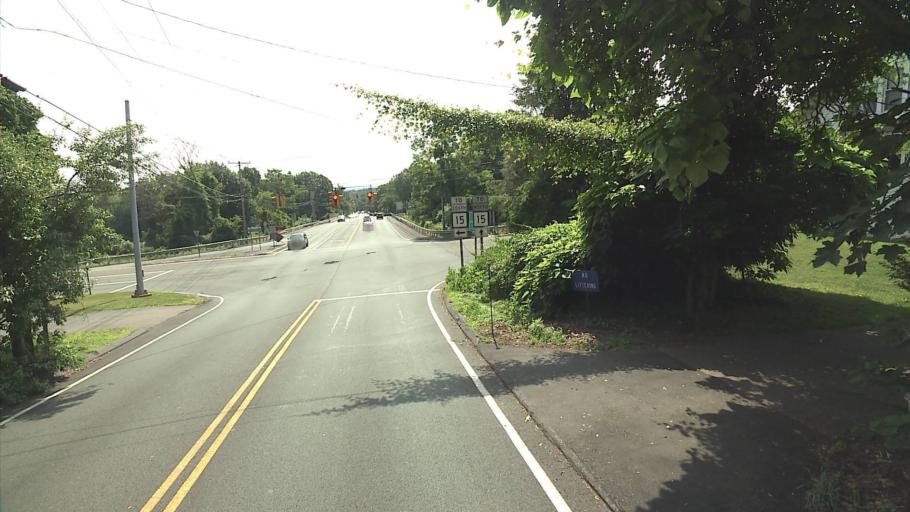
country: US
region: Connecticut
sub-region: New Haven County
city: North Haven
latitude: 41.3929
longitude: -72.8770
